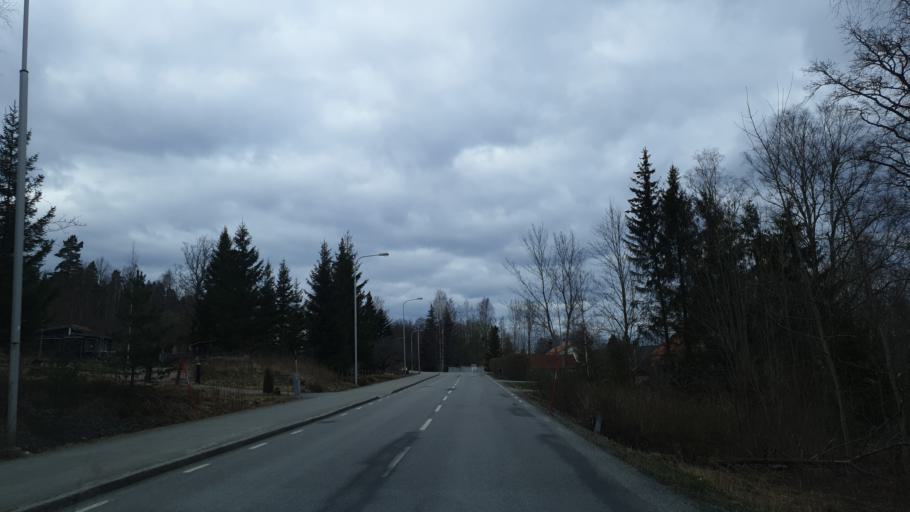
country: SE
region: OErebro
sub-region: Nora Kommun
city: Nora
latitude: 59.5345
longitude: 15.0330
